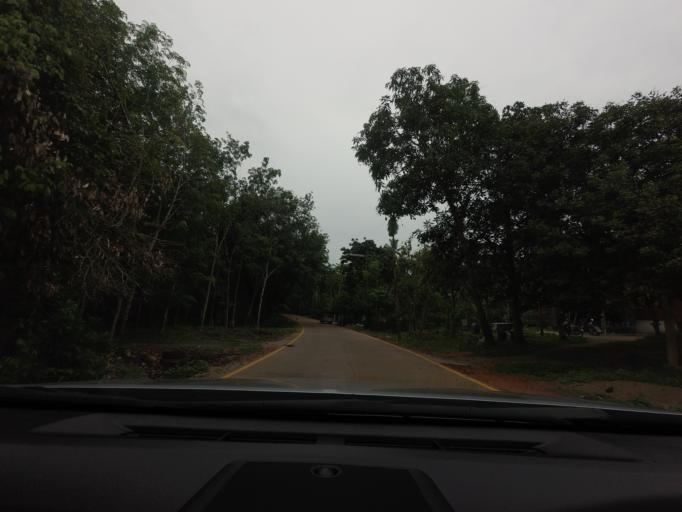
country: TH
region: Narathiwat
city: Rueso
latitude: 6.4092
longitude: 101.5275
